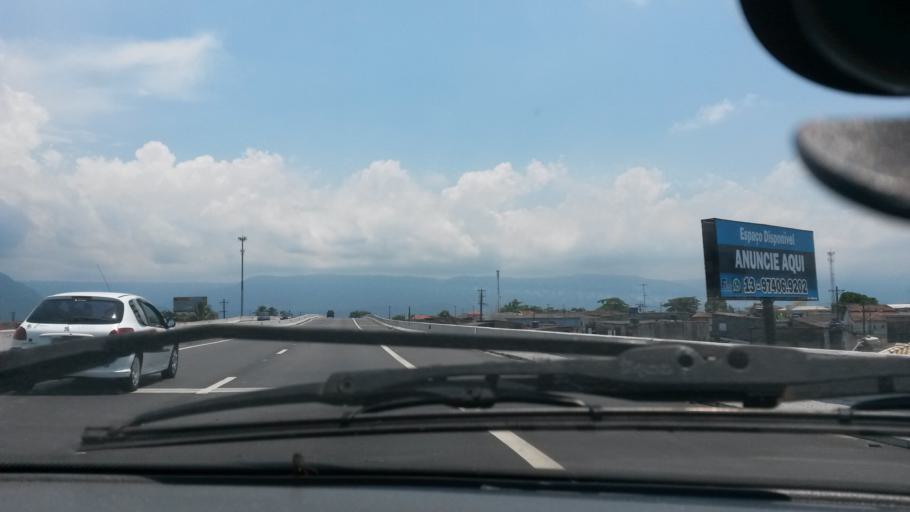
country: BR
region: Sao Paulo
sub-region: Sao Vicente
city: Sao Vicente
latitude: -23.9625
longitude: -46.4029
